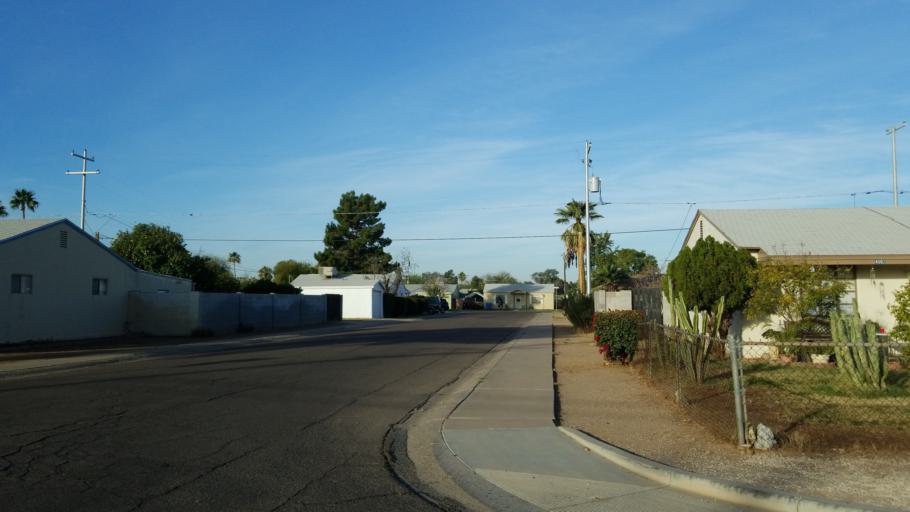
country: US
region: Arizona
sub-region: Maricopa County
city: Phoenix
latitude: 33.4933
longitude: -112.0870
